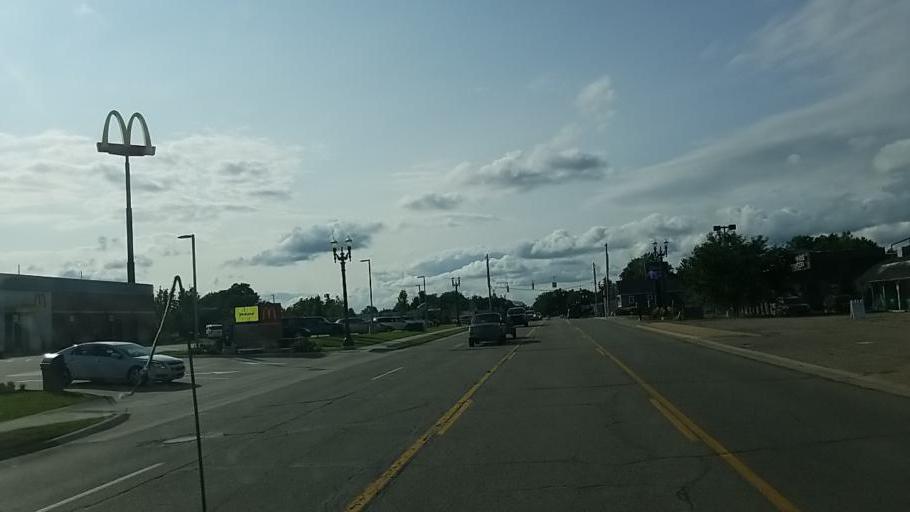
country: US
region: Michigan
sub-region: Ionia County
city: Portland
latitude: 42.8634
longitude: -84.8882
